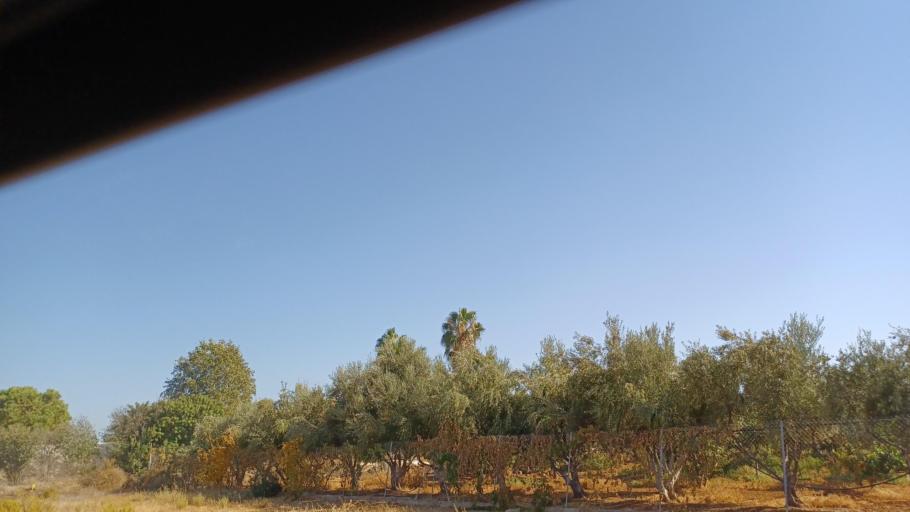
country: CY
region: Larnaka
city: Kolossi
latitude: 34.6693
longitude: 32.9500
